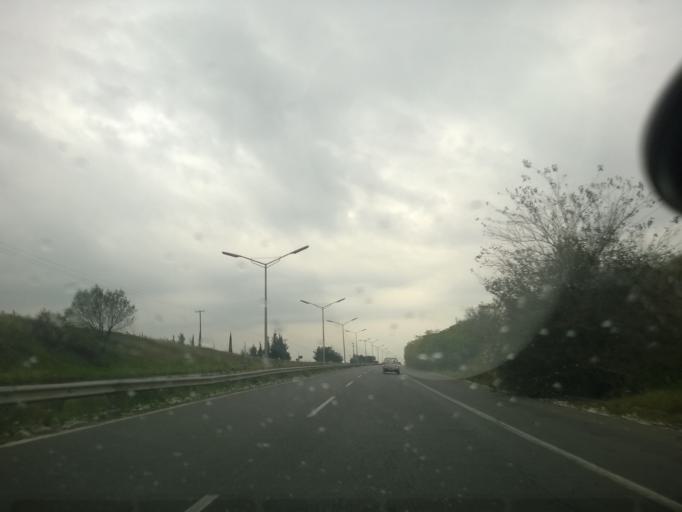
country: GR
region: Central Macedonia
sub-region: Nomos Thessalonikis
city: Agios Athanasios
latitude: 40.7107
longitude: 22.7594
